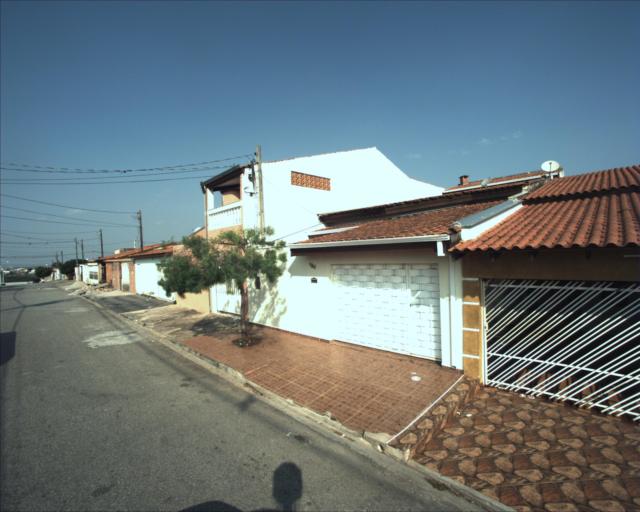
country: BR
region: Sao Paulo
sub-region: Sorocaba
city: Sorocaba
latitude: -23.4332
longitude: -47.4770
